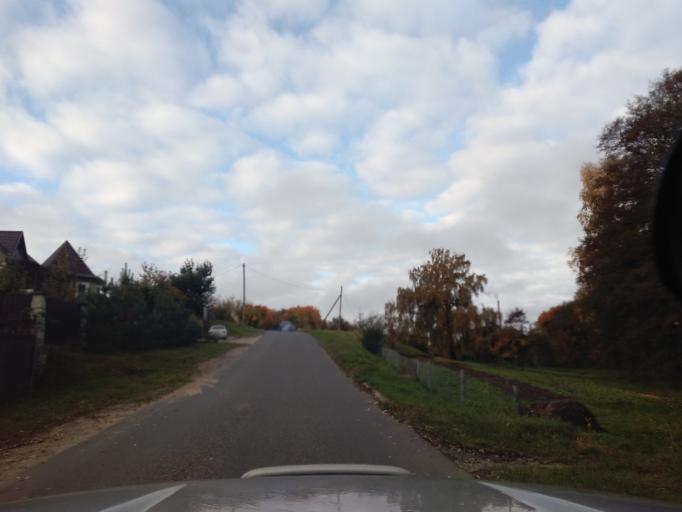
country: BY
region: Minsk
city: Kapyl'
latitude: 53.1574
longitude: 27.0878
